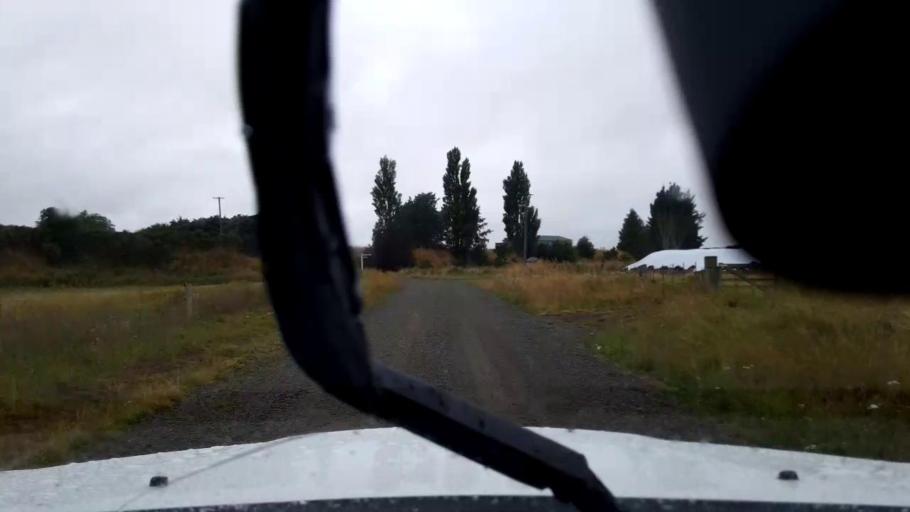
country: NZ
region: Canterbury
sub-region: Timaru District
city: Pleasant Point
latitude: -44.2533
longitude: 171.2174
